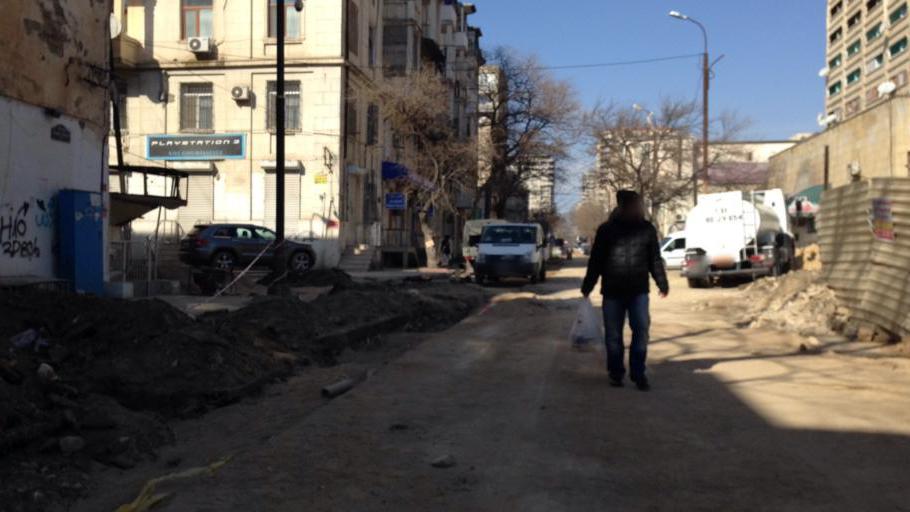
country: AZ
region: Baki
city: Baku
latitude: 40.3896
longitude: 49.8446
